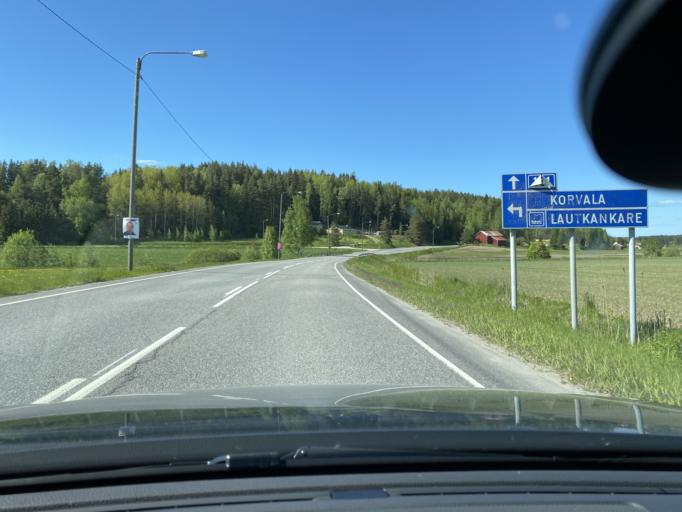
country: FI
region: Varsinais-Suomi
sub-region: Turku
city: Sauvo
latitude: 60.3539
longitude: 22.6701
